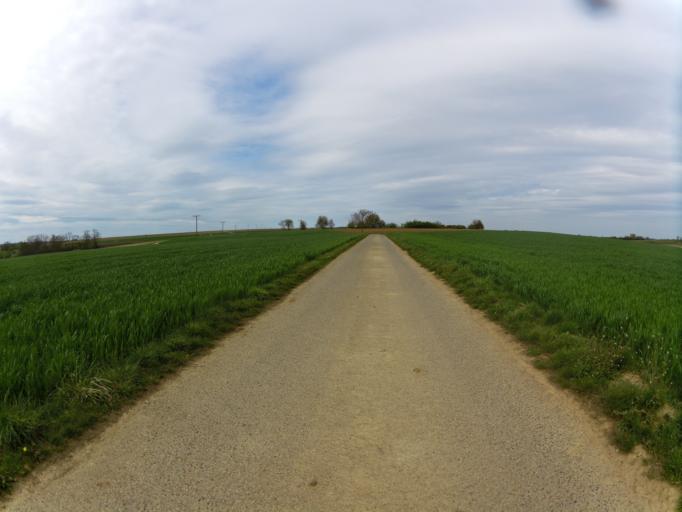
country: DE
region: Bavaria
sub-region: Regierungsbezirk Unterfranken
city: Prosselsheim
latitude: 49.8613
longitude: 10.1423
